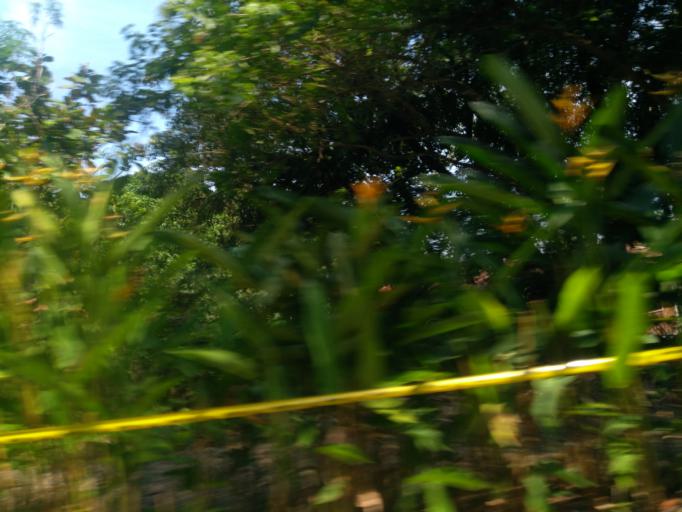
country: MY
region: Sarawak
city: Kuching
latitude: 1.7483
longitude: 110.3156
